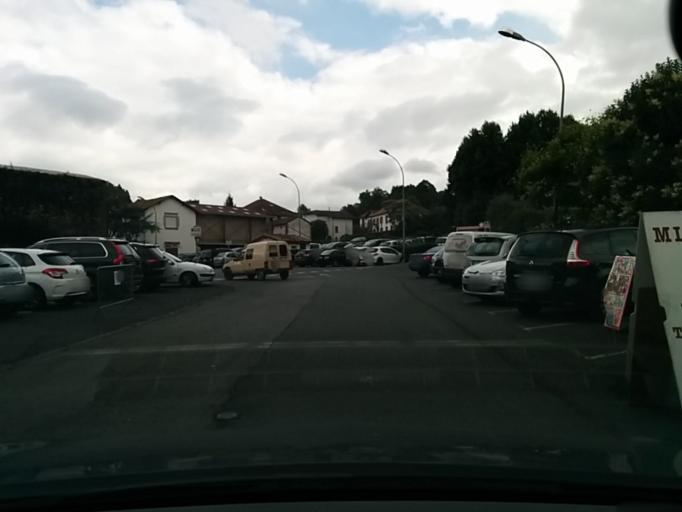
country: FR
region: Aquitaine
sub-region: Departement des Pyrenees-Atlantiques
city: Saint-Jean-Pied-de-Port
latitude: 43.1612
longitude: -1.2396
